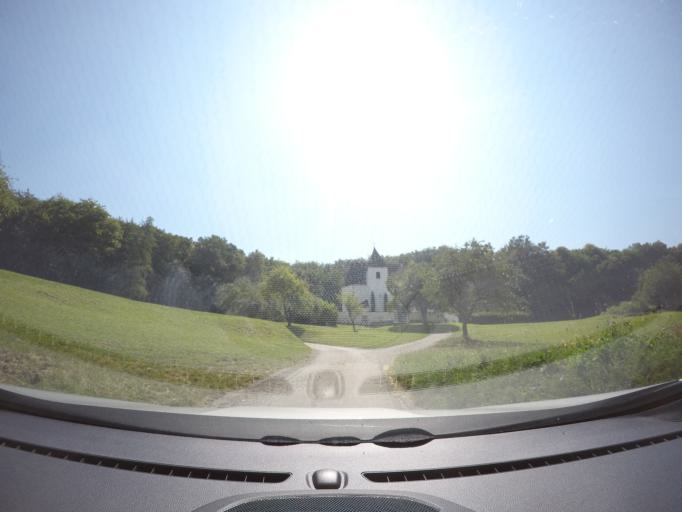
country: AT
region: Lower Austria
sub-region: Politischer Bezirk Sankt Polten
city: Maria-Anzbach
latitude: 48.2156
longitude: 15.9316
